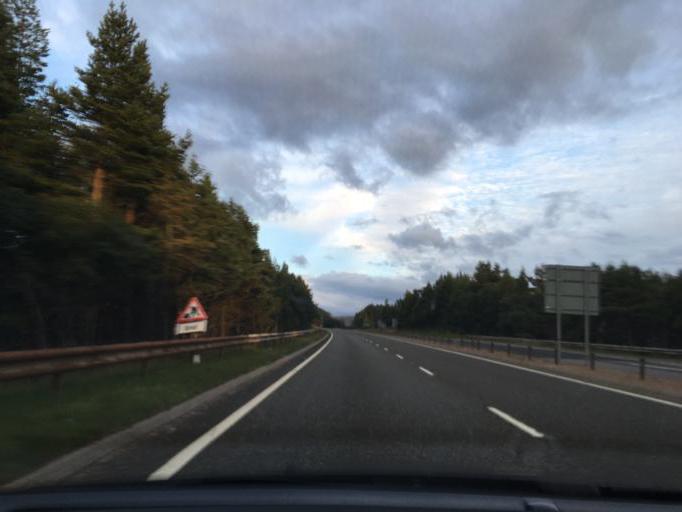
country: GB
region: Scotland
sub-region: Highland
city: Aviemore
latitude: 57.3422
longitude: -3.9954
